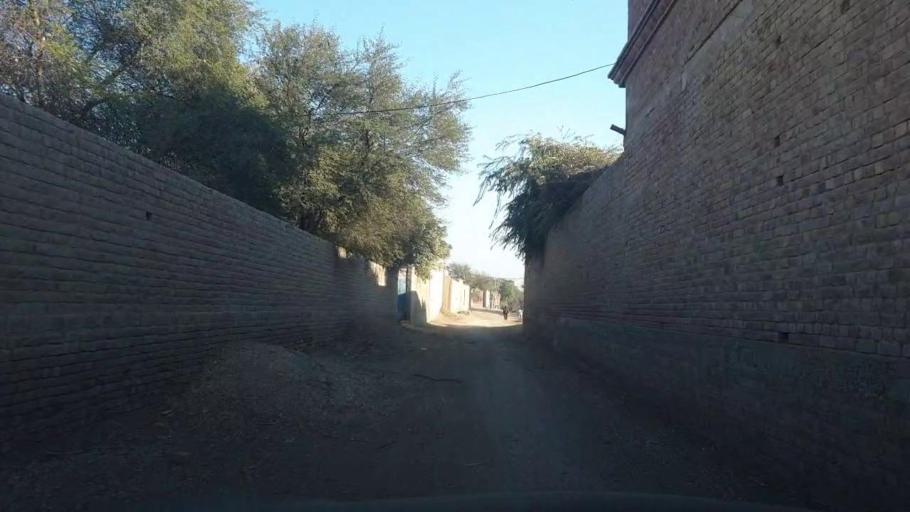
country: PK
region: Sindh
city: Ghotki
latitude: 28.0692
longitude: 69.3656
